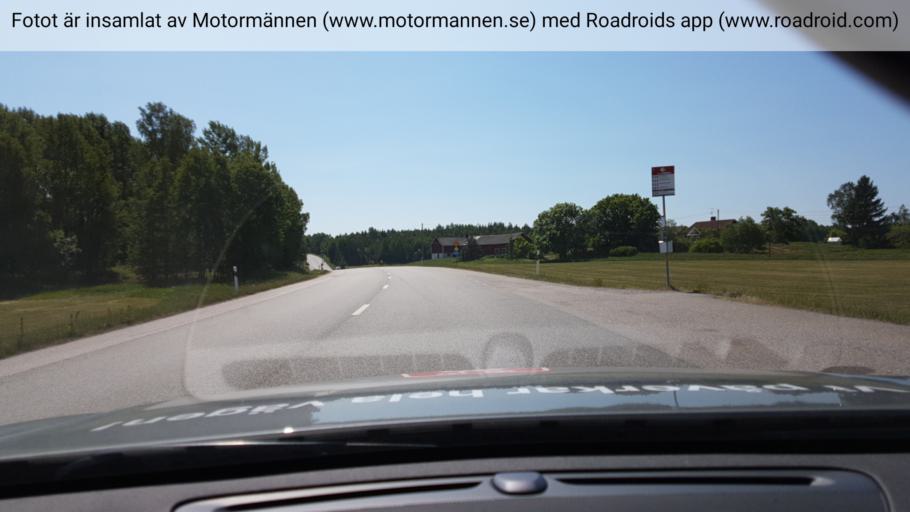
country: SE
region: Stockholm
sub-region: Norrtalje Kommun
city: Rimbo
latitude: 59.6481
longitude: 18.3352
